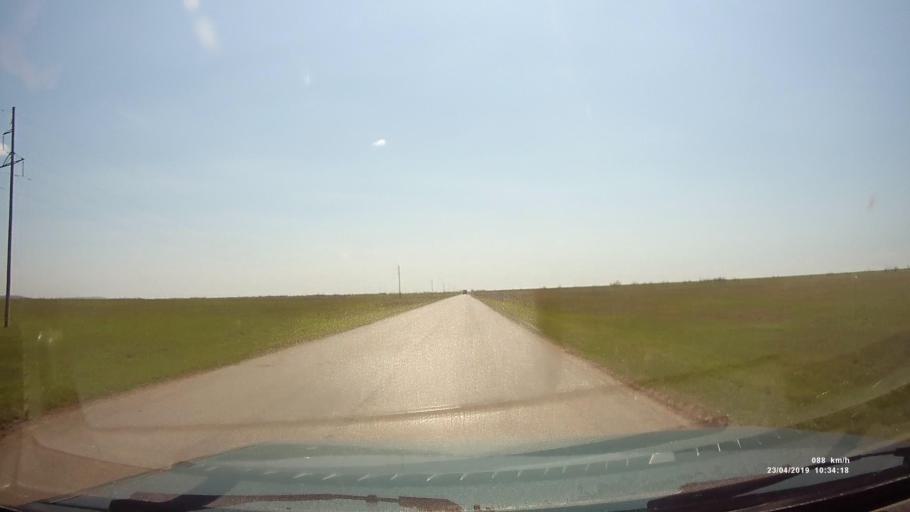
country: RU
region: Kalmykiya
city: Yashalta
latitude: 46.5658
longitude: 42.6078
